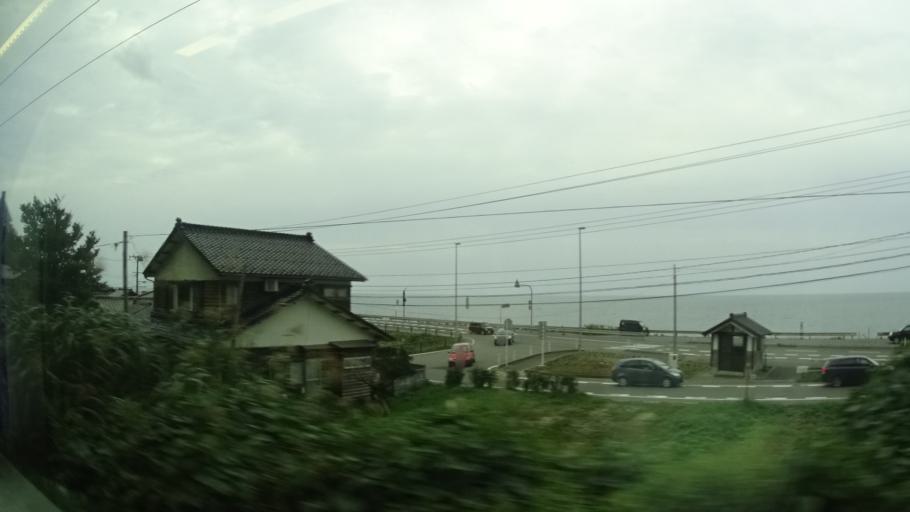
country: JP
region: Yamagata
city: Tsuruoka
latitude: 38.6036
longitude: 139.5727
